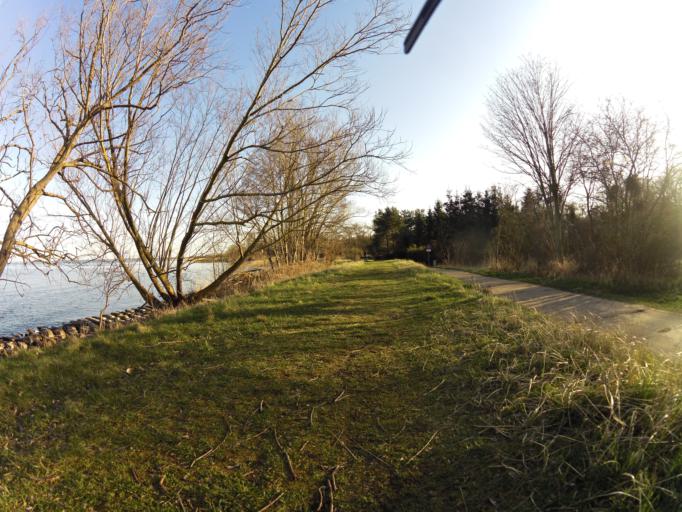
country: PL
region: West Pomeranian Voivodeship
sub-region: Powiat policki
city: Nowe Warpno
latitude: 53.7323
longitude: 14.3322
